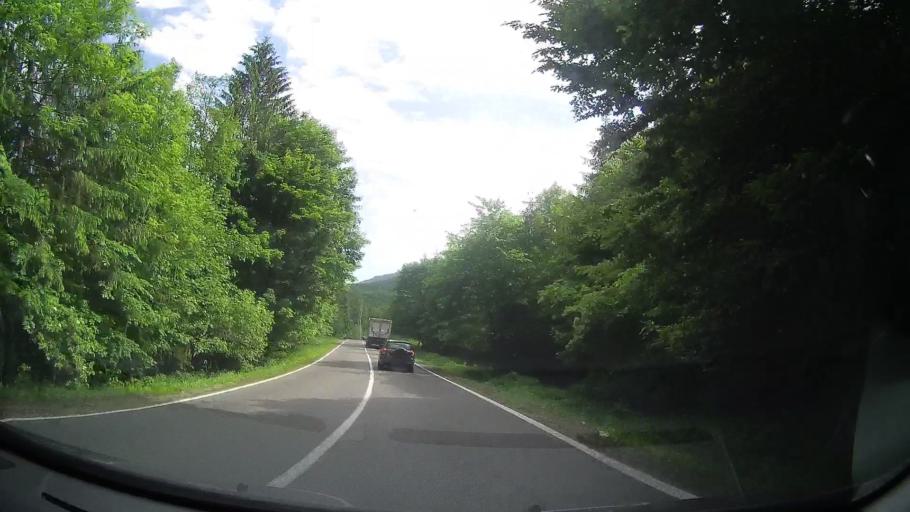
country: RO
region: Prahova
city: Maneciu
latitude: 45.3727
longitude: 25.9299
